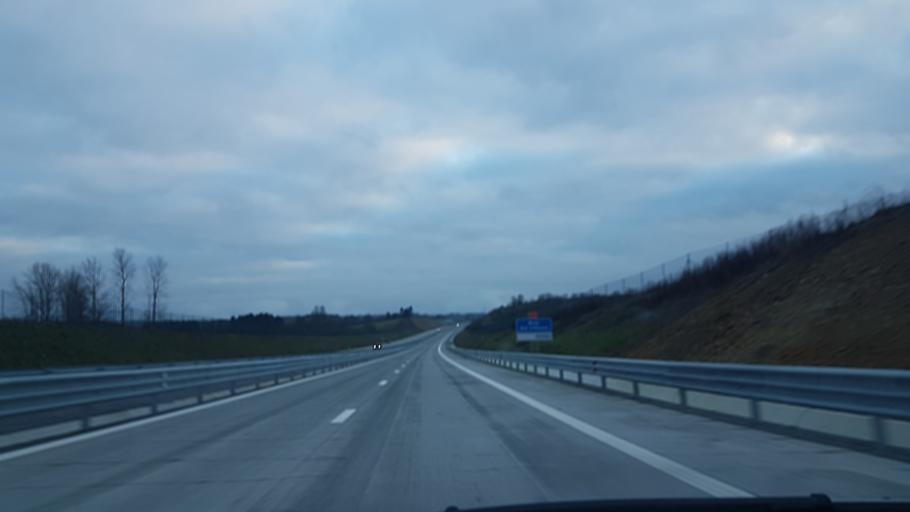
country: FR
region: Champagne-Ardenne
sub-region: Departement des Ardennes
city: Rocroi
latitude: 49.9757
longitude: 4.5387
